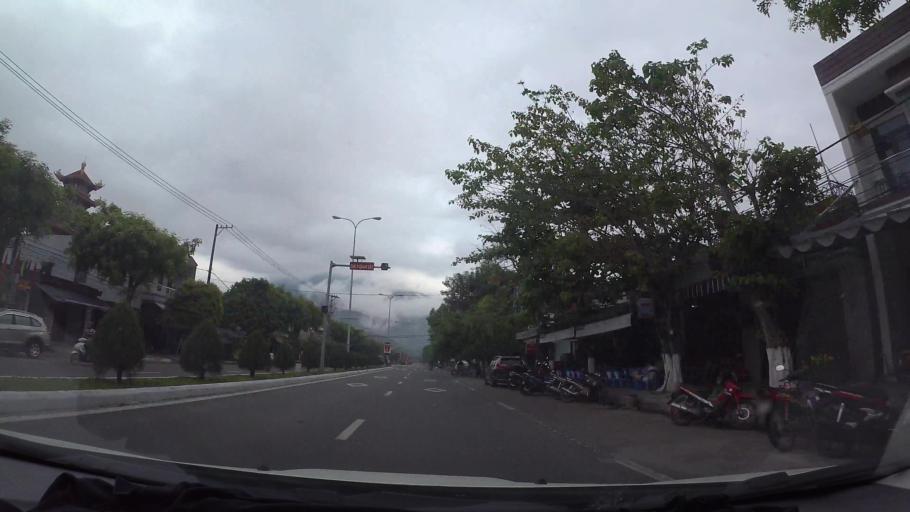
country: VN
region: Da Nang
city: Lien Chieu
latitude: 16.1350
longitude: 108.1197
